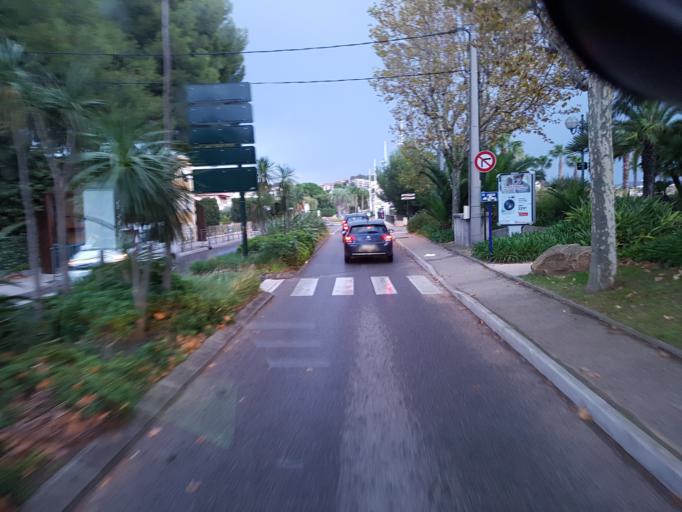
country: FR
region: Provence-Alpes-Cote d'Azur
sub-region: Departement du Var
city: Sanary-sur-Mer
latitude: 43.1161
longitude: 5.8063
